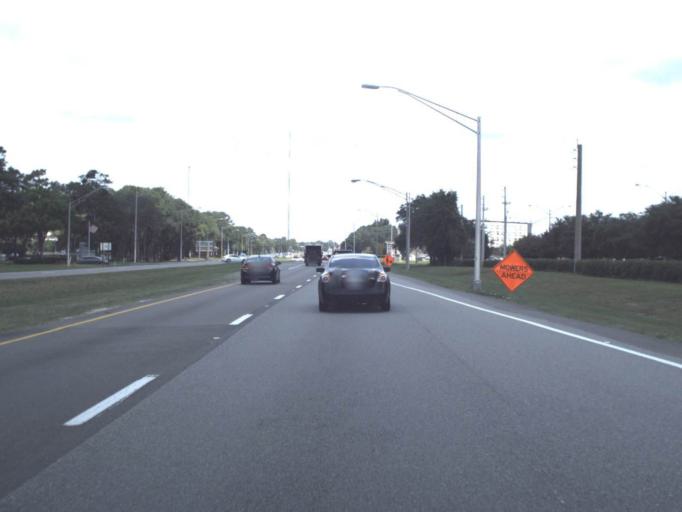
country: US
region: Florida
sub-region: Duval County
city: Jacksonville
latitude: 30.2553
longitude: -81.5539
